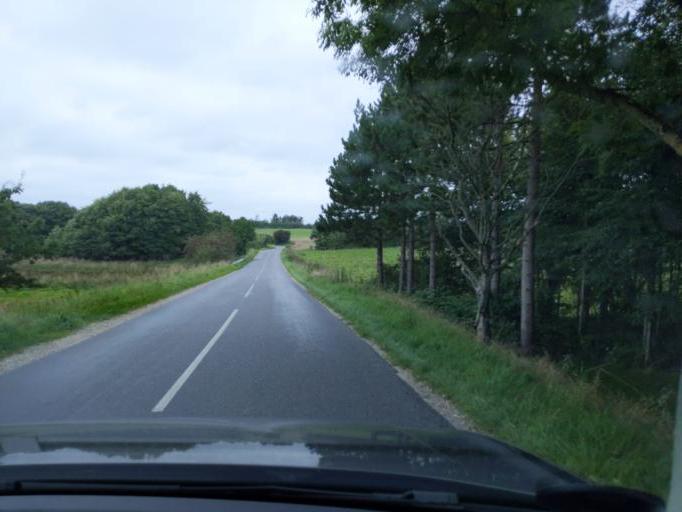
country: DK
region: North Denmark
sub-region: Mariagerfjord Kommune
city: Hobro
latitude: 56.5608
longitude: 9.7148
